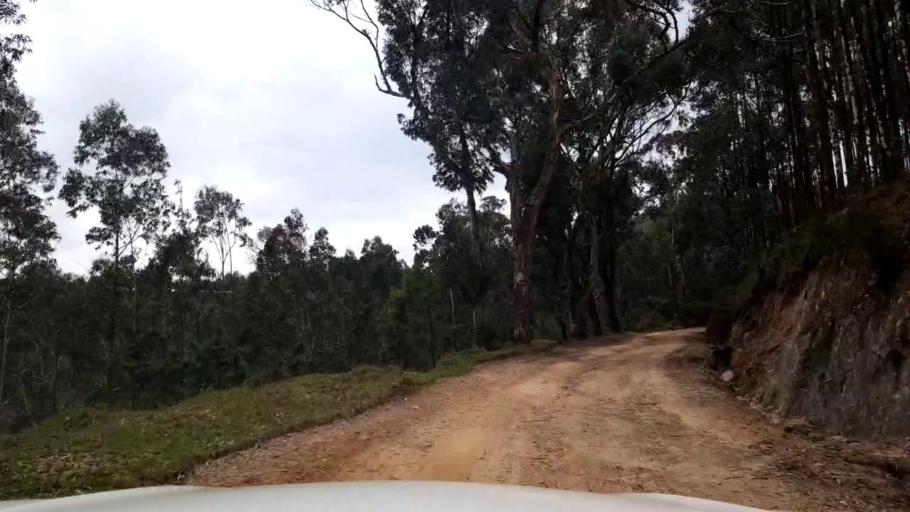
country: RW
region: Western Province
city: Kibuye
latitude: -1.9576
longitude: 29.3991
